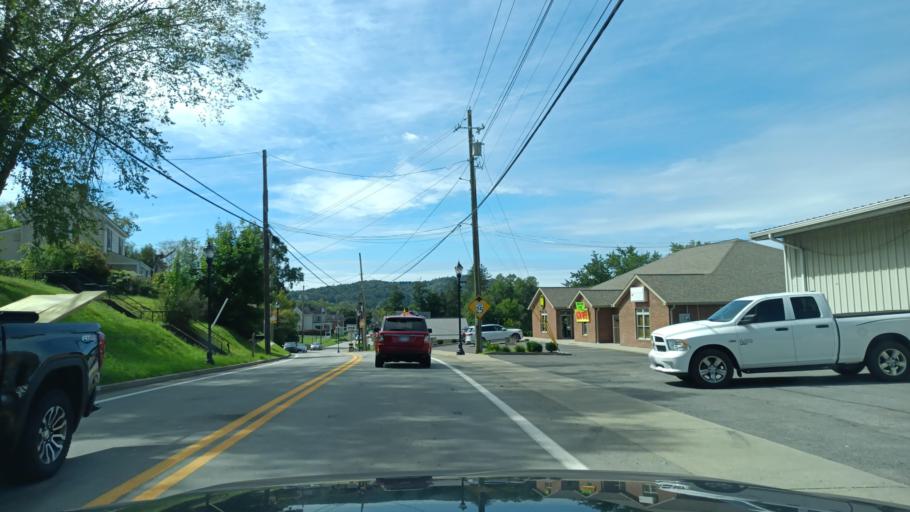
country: US
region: West Virginia
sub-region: Harrison County
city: Bridgeport
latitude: 39.2889
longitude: -80.2433
